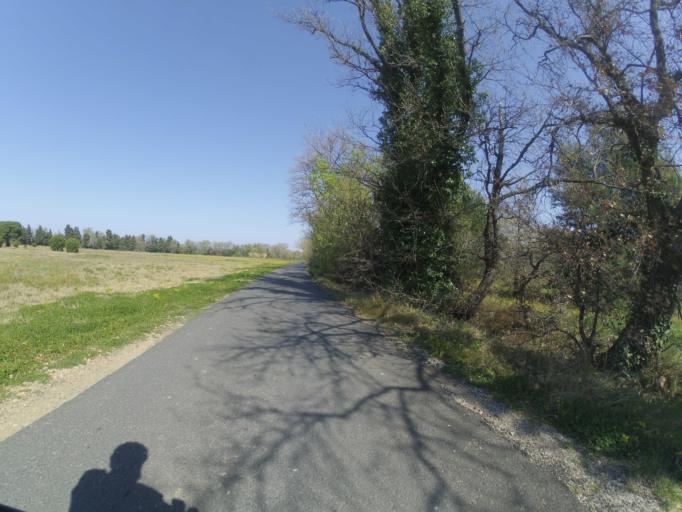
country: FR
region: Languedoc-Roussillon
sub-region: Departement des Pyrenees-Orientales
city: Thuir
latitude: 42.6584
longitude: 2.7598
